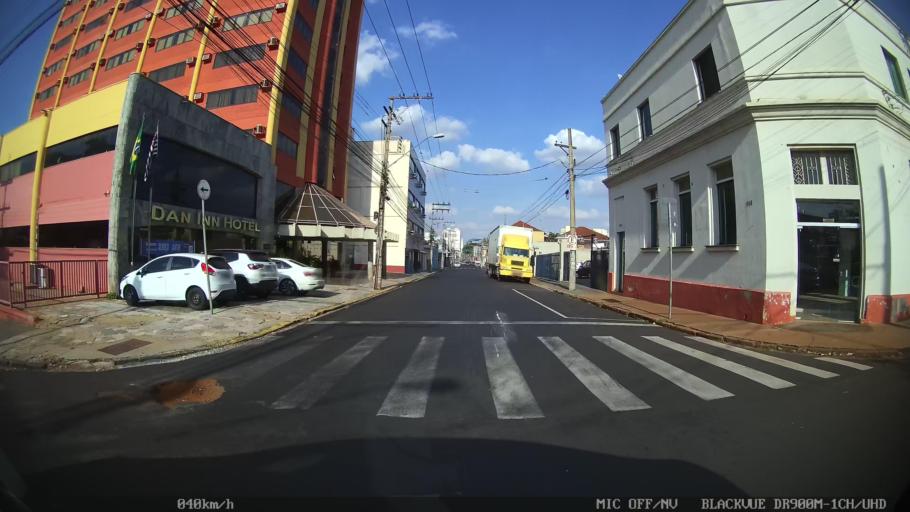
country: BR
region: Sao Paulo
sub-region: Ribeirao Preto
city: Ribeirao Preto
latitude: -21.1690
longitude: -47.8164
